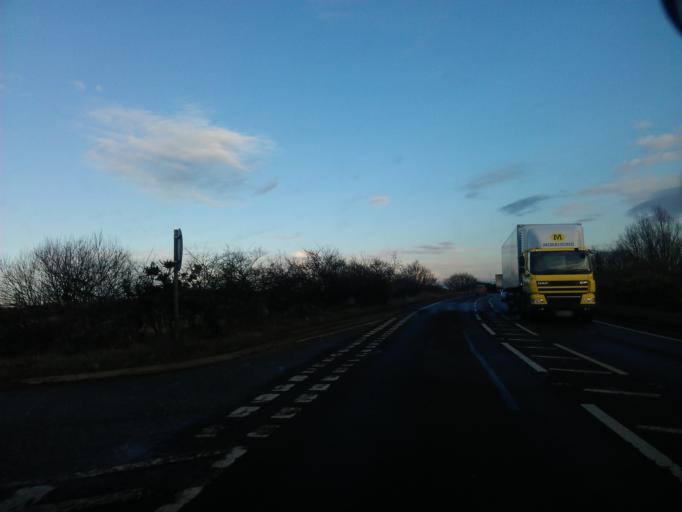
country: GB
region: England
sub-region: Suffolk
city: Shotley Gate
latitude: 51.9355
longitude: 1.2302
